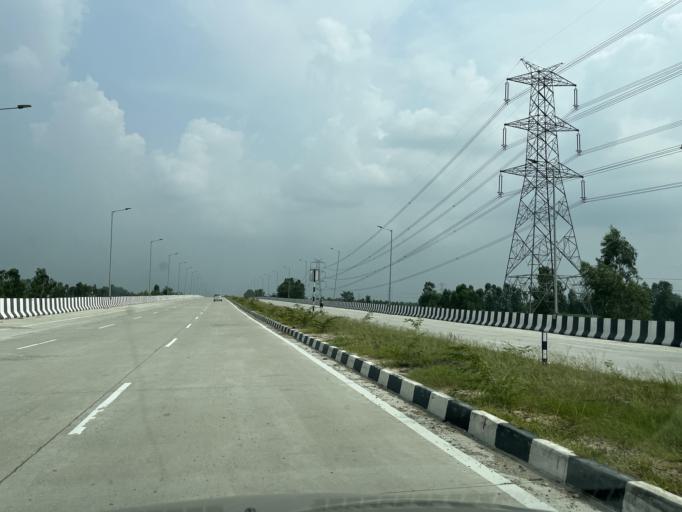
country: IN
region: Uttarakhand
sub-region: Udham Singh Nagar
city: Jaspur
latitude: 29.2968
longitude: 78.8388
